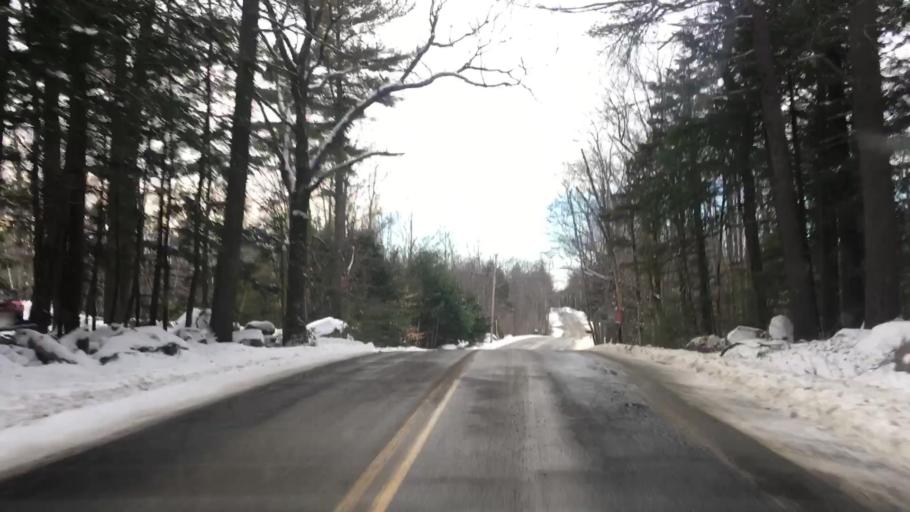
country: US
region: Maine
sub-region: Kennebec County
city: Chelsea
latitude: 44.2522
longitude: -69.7288
